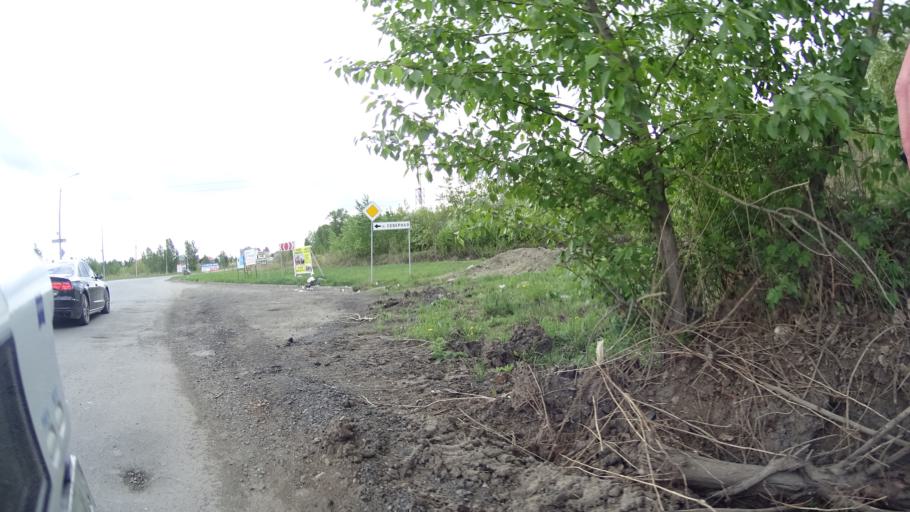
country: RU
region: Chelyabinsk
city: Sargazy
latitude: 55.1591
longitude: 61.2856
